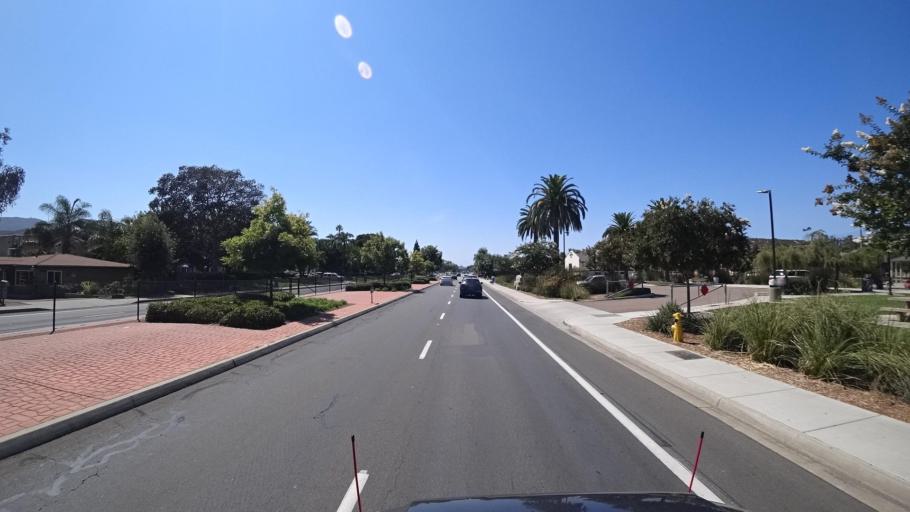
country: US
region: California
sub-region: San Diego County
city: San Marcos
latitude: 33.1401
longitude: -117.1685
